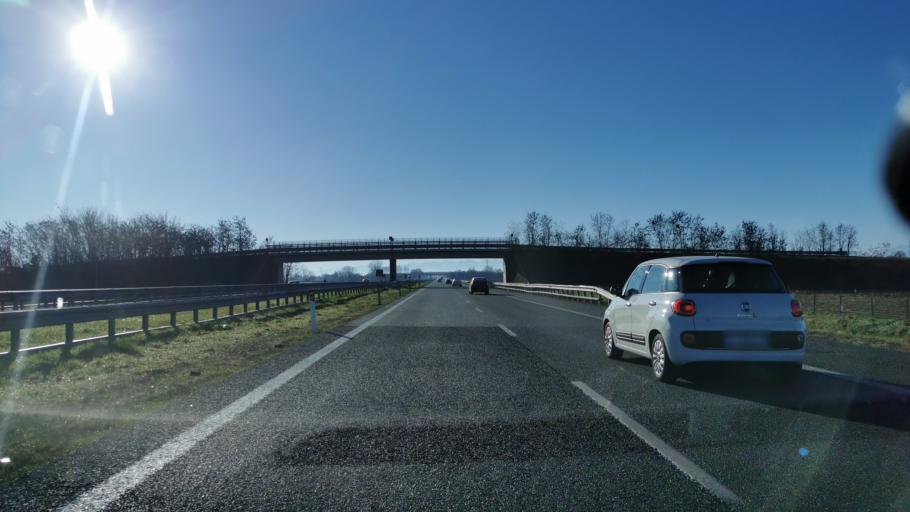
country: IT
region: Piedmont
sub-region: Provincia di Torino
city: Carmagnola
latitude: 44.8299
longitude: 7.7501
